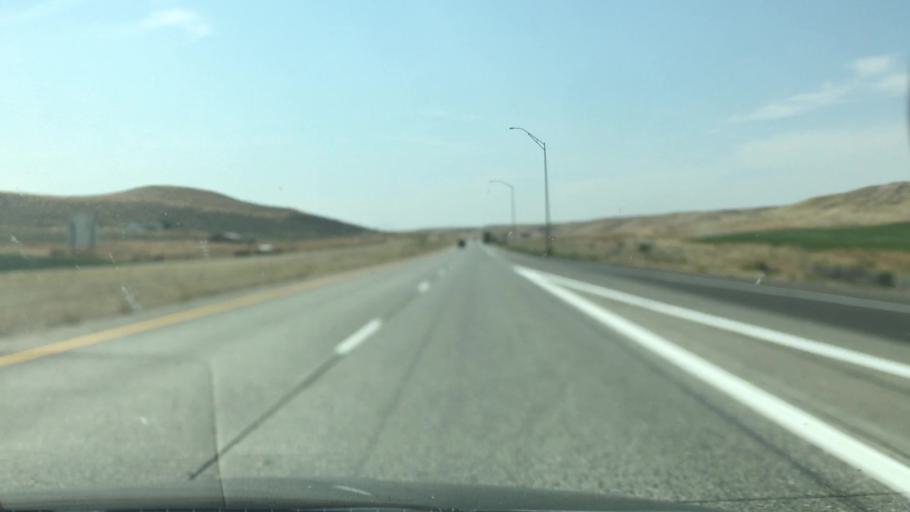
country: US
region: Idaho
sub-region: Elmore County
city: Glenns Ferry
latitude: 42.9624
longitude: -115.3140
